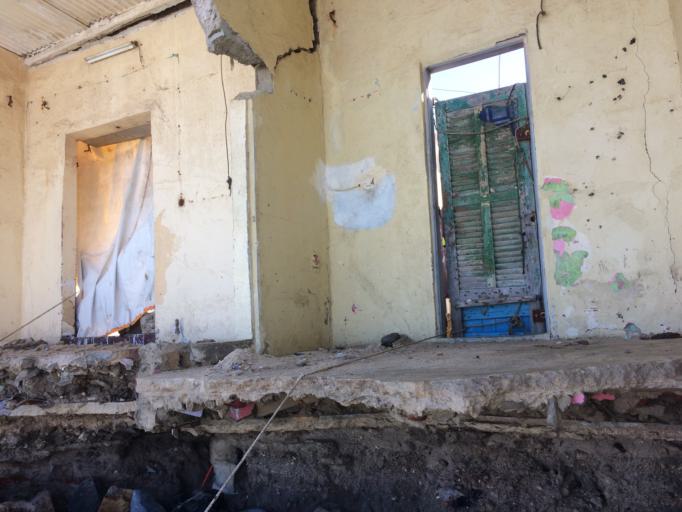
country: SN
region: Saint-Louis
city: Saint-Louis
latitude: 16.0244
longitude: -16.5092
